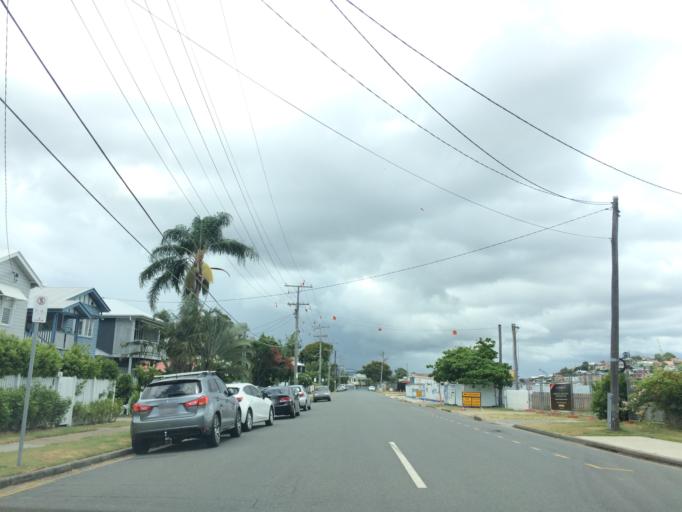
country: AU
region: Queensland
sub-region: Brisbane
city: Ascot
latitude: -27.4439
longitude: 153.0635
